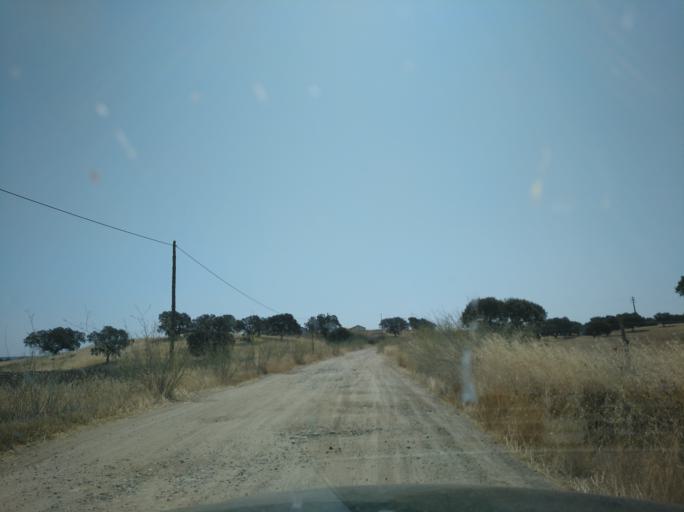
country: PT
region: Portalegre
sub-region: Campo Maior
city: Campo Maior
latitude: 39.0313
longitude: -6.9806
